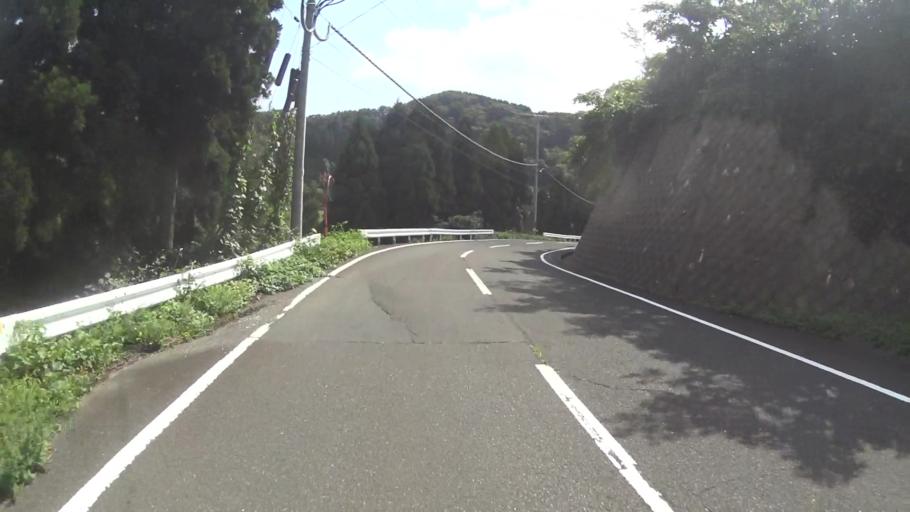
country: JP
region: Kyoto
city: Miyazu
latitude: 35.7215
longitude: 135.1870
